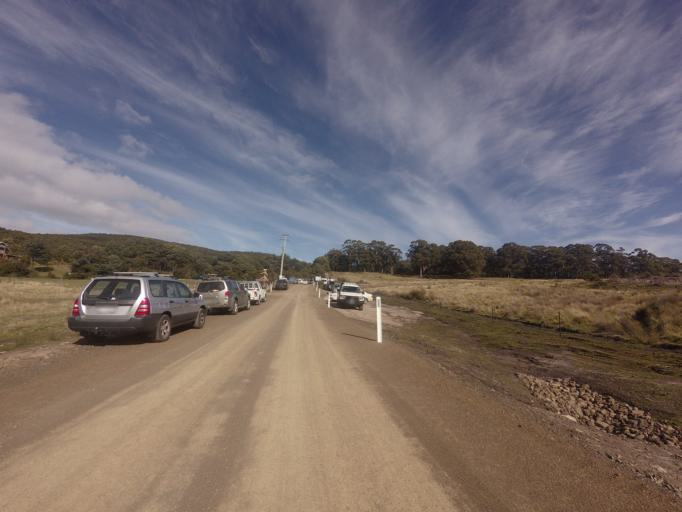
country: AU
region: Tasmania
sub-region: Clarence
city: Sandford
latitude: -43.1940
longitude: 147.7774
